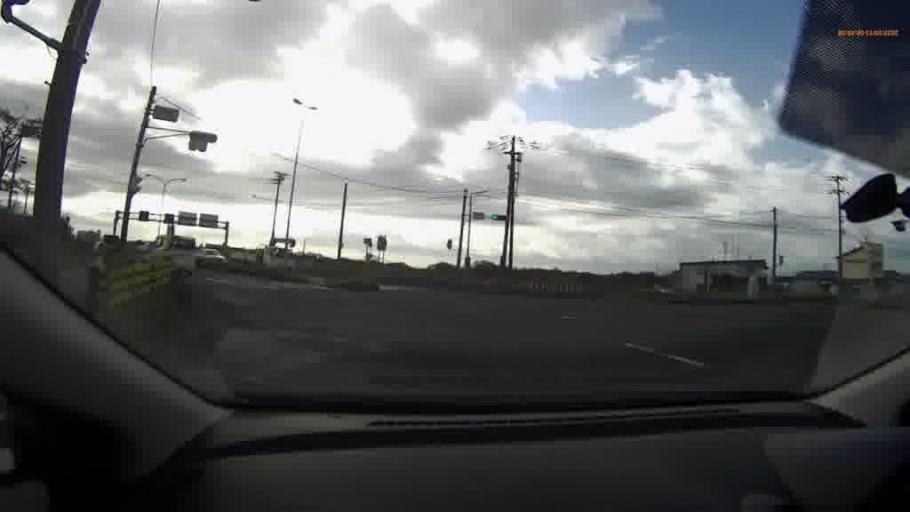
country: JP
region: Hokkaido
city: Kushiro
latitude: 43.0121
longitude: 144.2658
